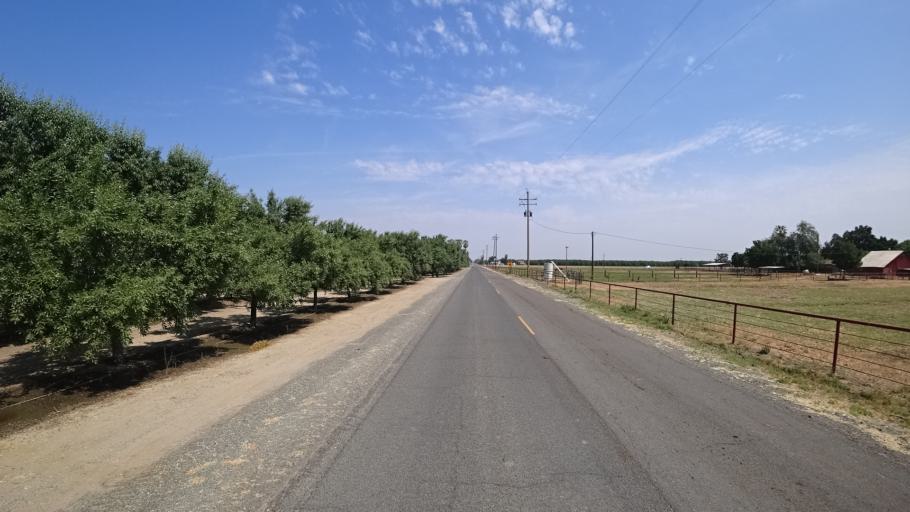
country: US
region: California
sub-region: Kings County
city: Armona
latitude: 36.3404
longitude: -119.7448
